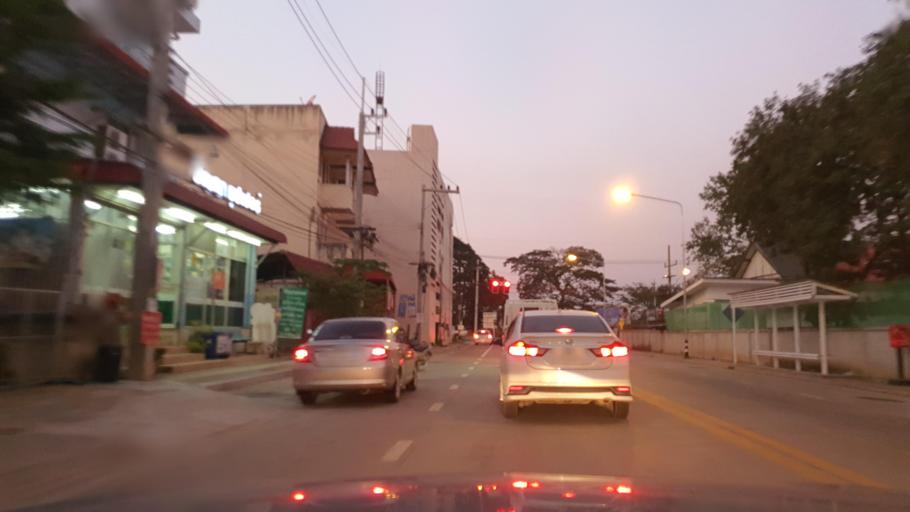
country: TH
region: Phayao
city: Dok Kham Tai
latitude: 19.1621
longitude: 99.9923
